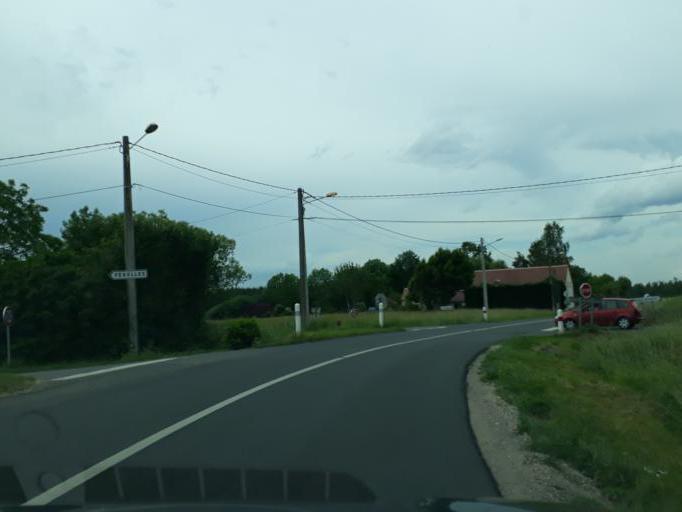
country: FR
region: Centre
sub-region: Departement du Loiret
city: Ferolles
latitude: 47.8374
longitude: 2.1388
